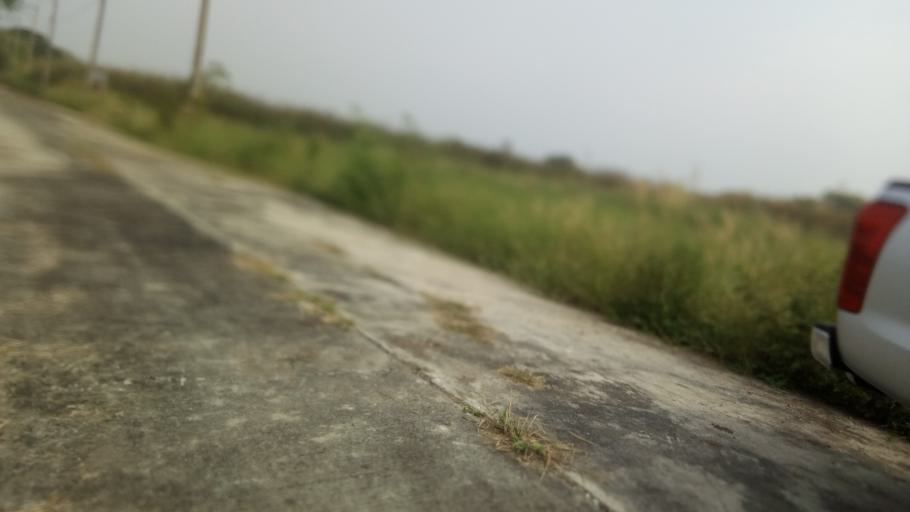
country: TH
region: Pathum Thani
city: Nong Suea
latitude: 14.0497
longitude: 100.8467
